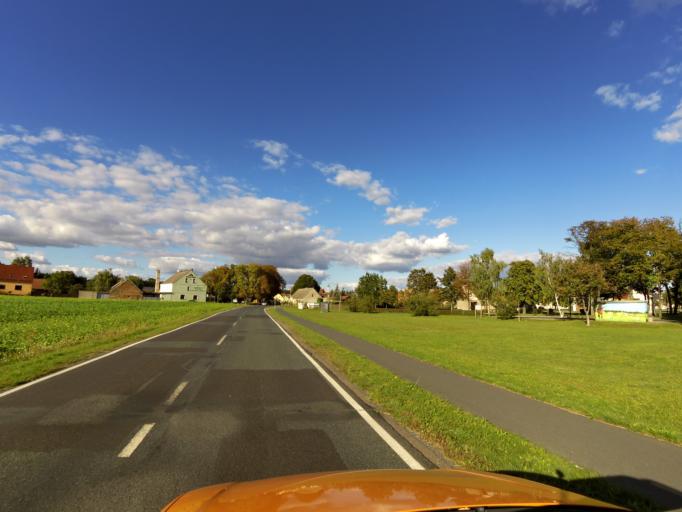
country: DE
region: Brandenburg
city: Luckenwalde
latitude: 52.1254
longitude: 13.1671
